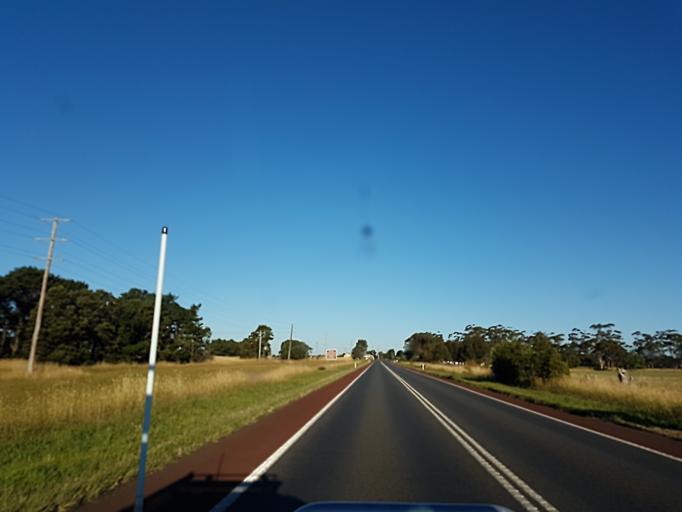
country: AU
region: Victoria
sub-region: Warrnambool
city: Allansford
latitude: -38.2144
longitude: 143.0084
